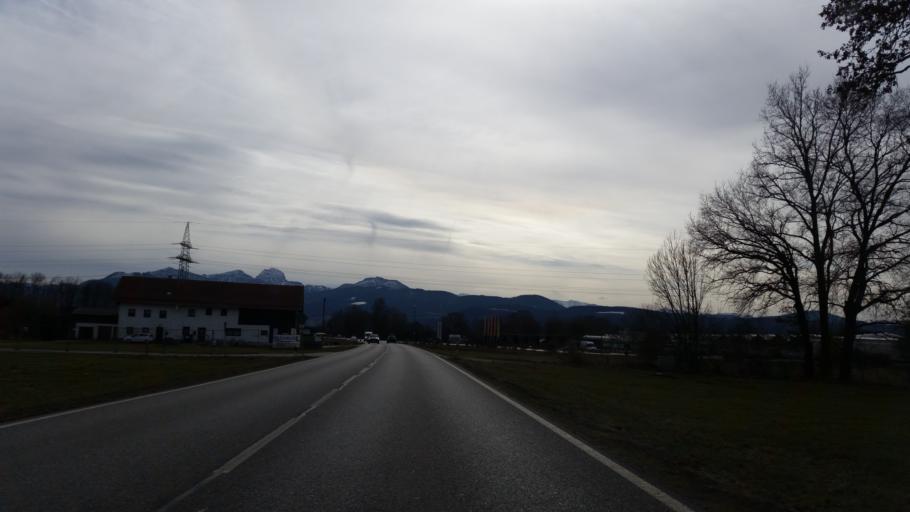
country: DE
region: Bavaria
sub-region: Upper Bavaria
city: Bad Aibling
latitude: 47.8429
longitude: 12.0124
